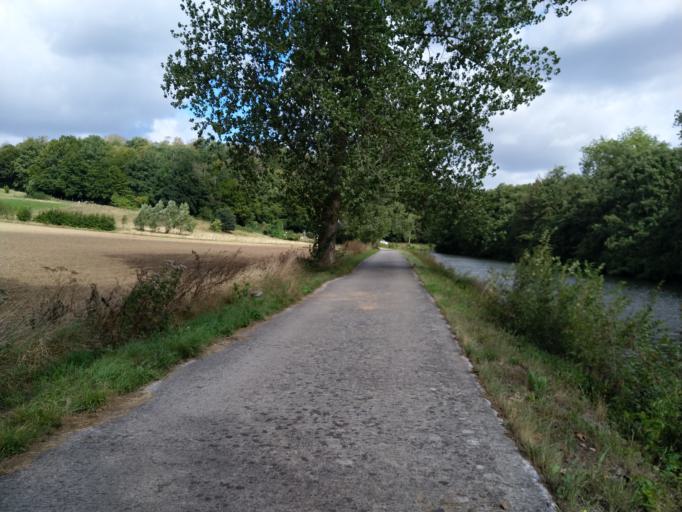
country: BE
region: Wallonia
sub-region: Province du Hainaut
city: Lobbes
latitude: 50.3464
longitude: 4.2480
